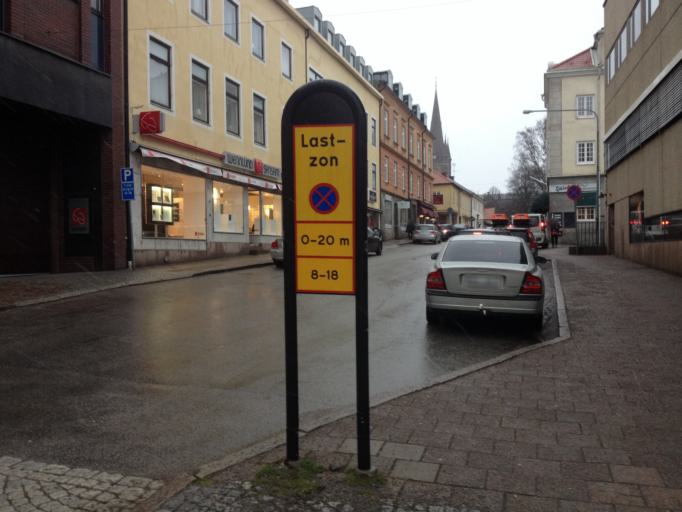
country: SE
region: Vaestra Goetaland
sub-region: Mariestads Kommun
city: Mariestad
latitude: 58.7097
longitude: 13.8228
